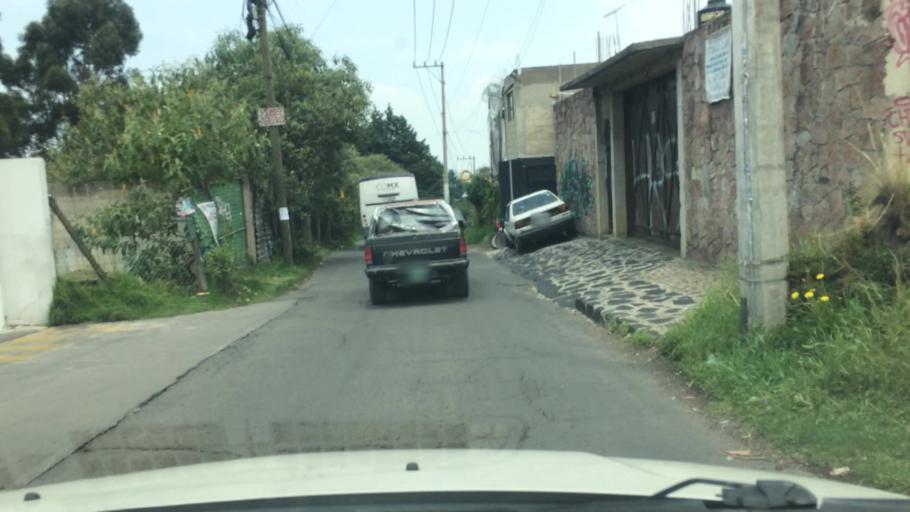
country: MX
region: Mexico City
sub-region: Tlalpan
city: Lomas de Tepemecatl
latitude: 19.2254
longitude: -99.2114
